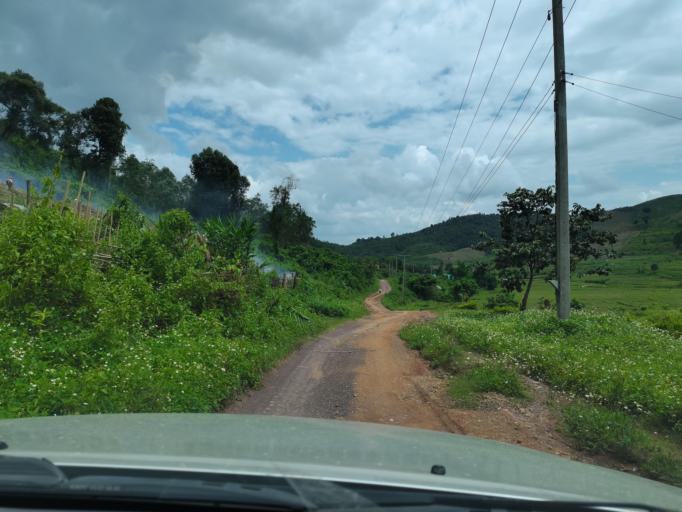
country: LA
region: Loungnamtha
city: Muang Long
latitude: 20.7092
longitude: 101.0109
